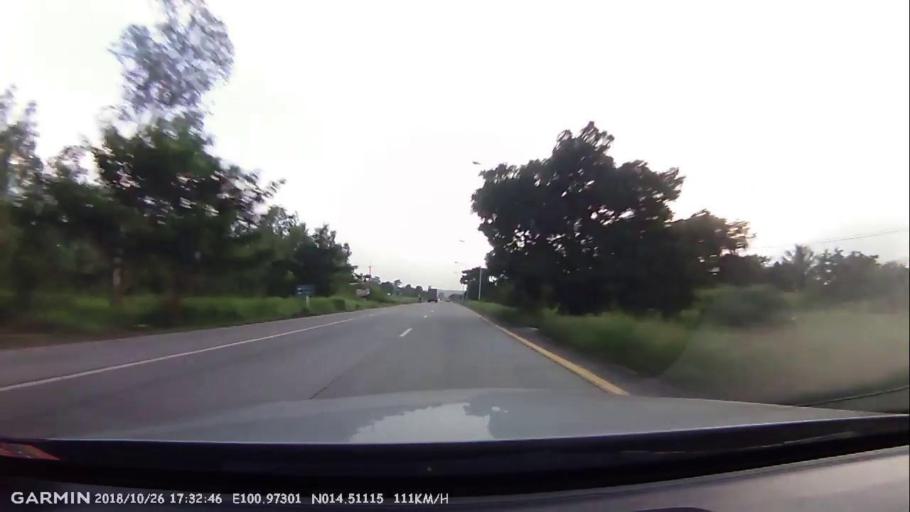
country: TH
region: Sara Buri
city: Saraburi
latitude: 14.5109
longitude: 100.9730
